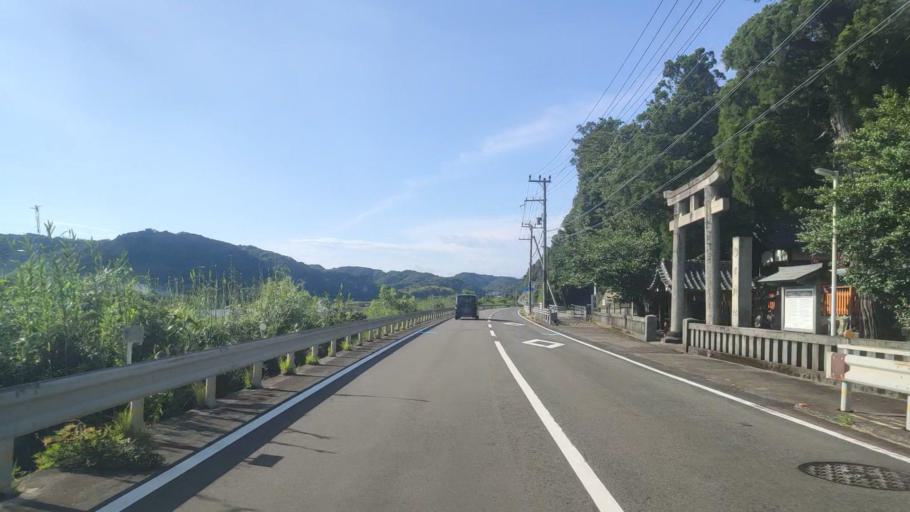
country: JP
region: Wakayama
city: Tanabe
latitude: 33.6548
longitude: 135.4021
